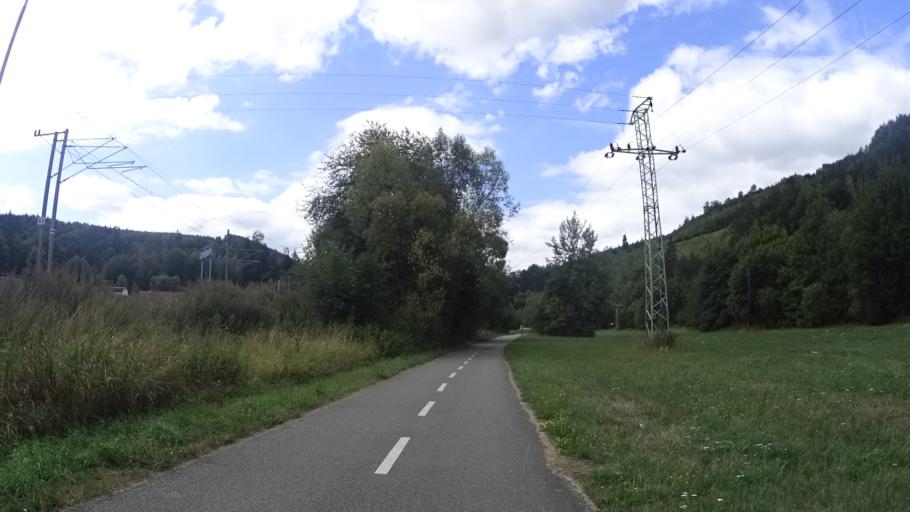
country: CZ
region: Pardubicky
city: Dolni Dobrouc
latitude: 49.9943
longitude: 16.4493
